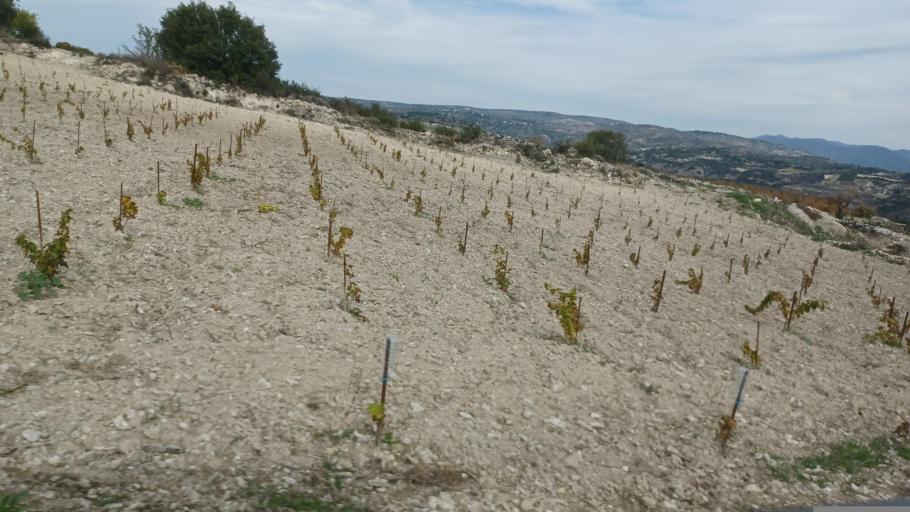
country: CY
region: Pafos
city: Mesogi
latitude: 34.8585
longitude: 32.5240
